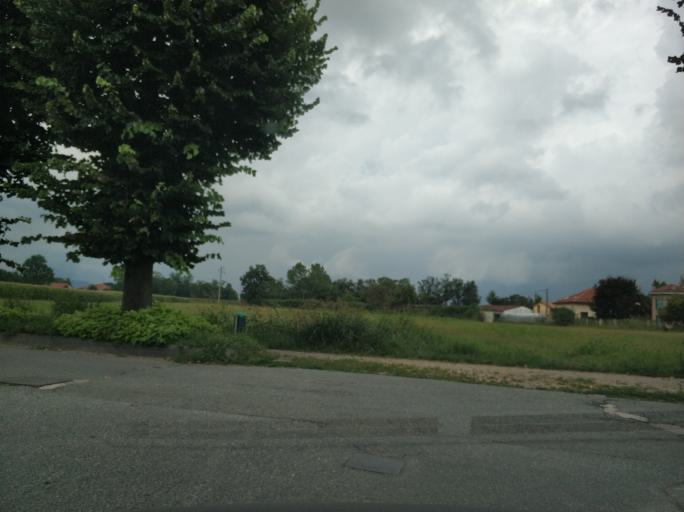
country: IT
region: Piedmont
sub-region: Provincia di Torino
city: Caselle Torinese
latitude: 45.1781
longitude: 7.6323
